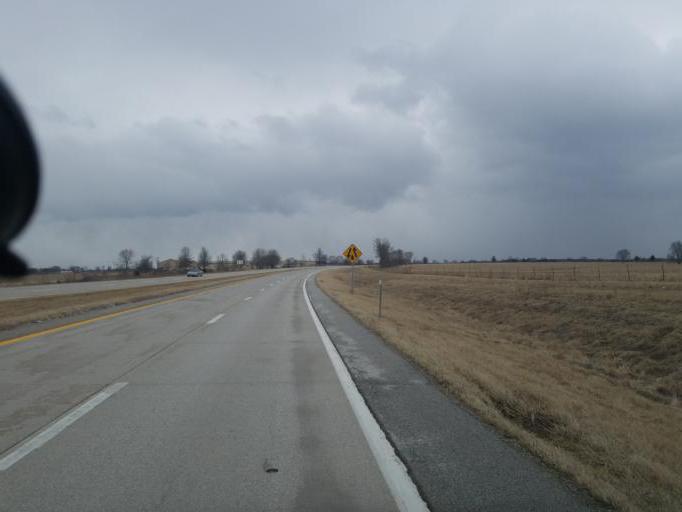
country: US
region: Missouri
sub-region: Macon County
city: Macon
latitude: 39.8011
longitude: -92.4750
